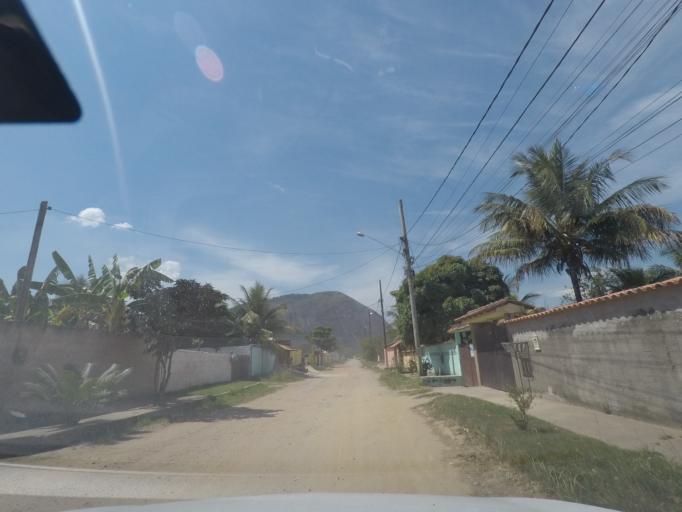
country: BR
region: Rio de Janeiro
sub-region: Marica
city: Marica
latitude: -22.9561
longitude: -42.9604
